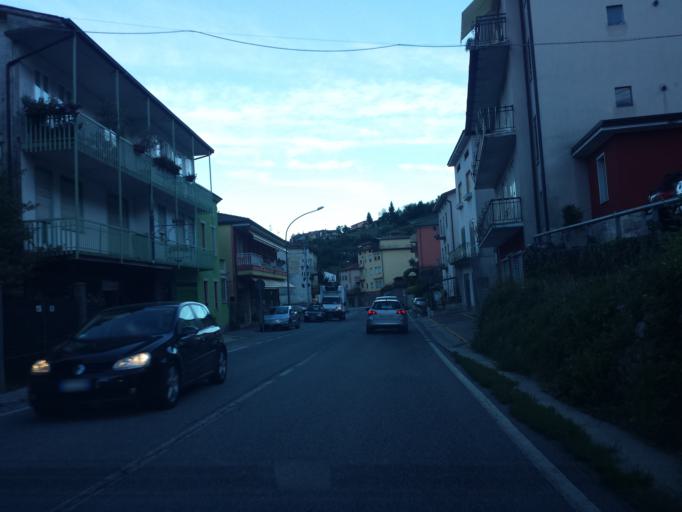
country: IT
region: Veneto
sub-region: Provincia di Vicenza
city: San Quirico
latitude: 45.6883
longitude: 11.2633
